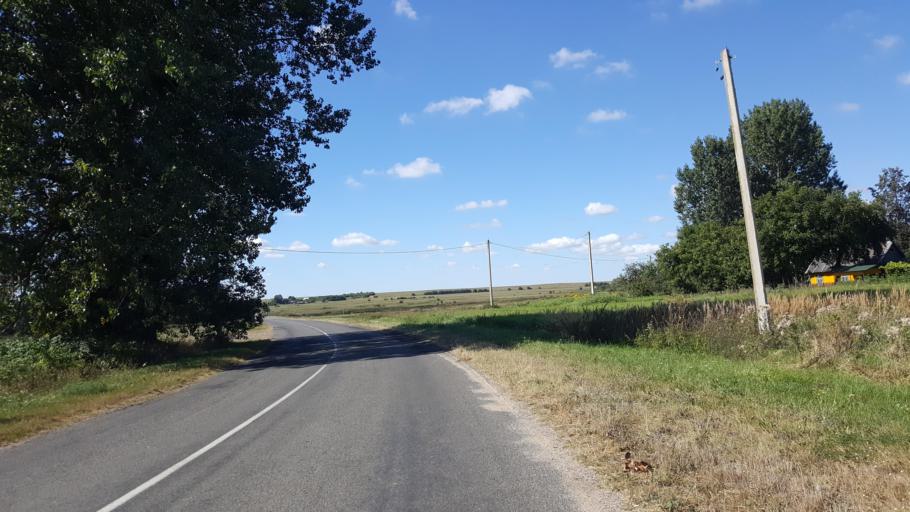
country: BY
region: Brest
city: Vysokaye
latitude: 52.3658
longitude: 23.5212
